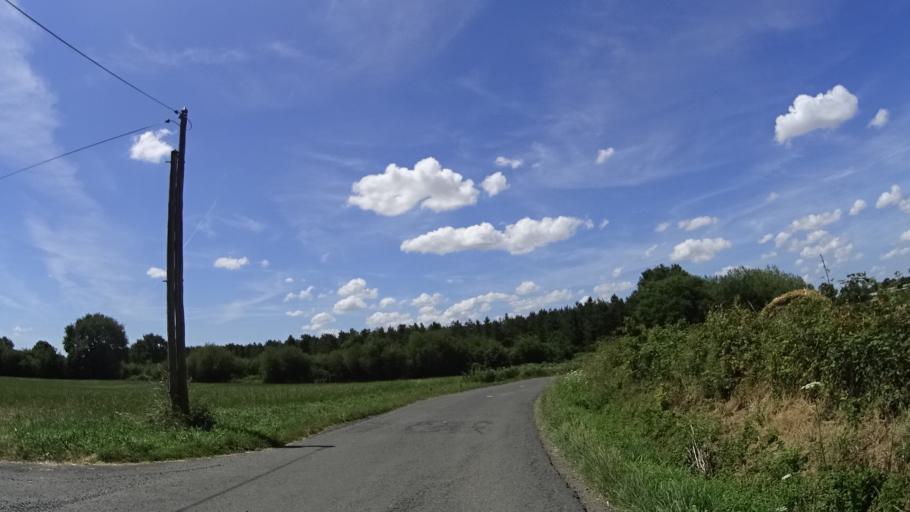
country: FR
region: Pays de la Loire
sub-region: Departement de Maine-et-Loire
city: Segre
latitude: 47.6353
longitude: -0.8716
